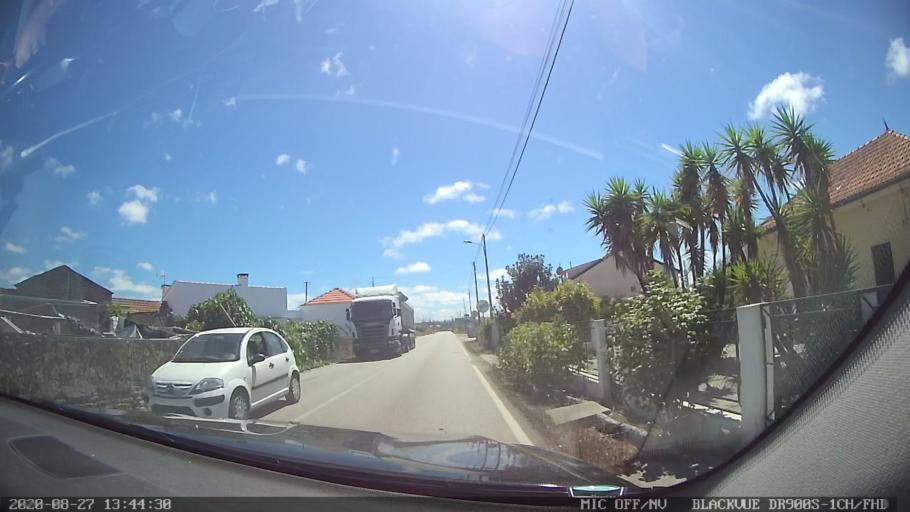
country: PT
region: Coimbra
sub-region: Mira
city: Mira
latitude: 40.4136
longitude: -8.7354
